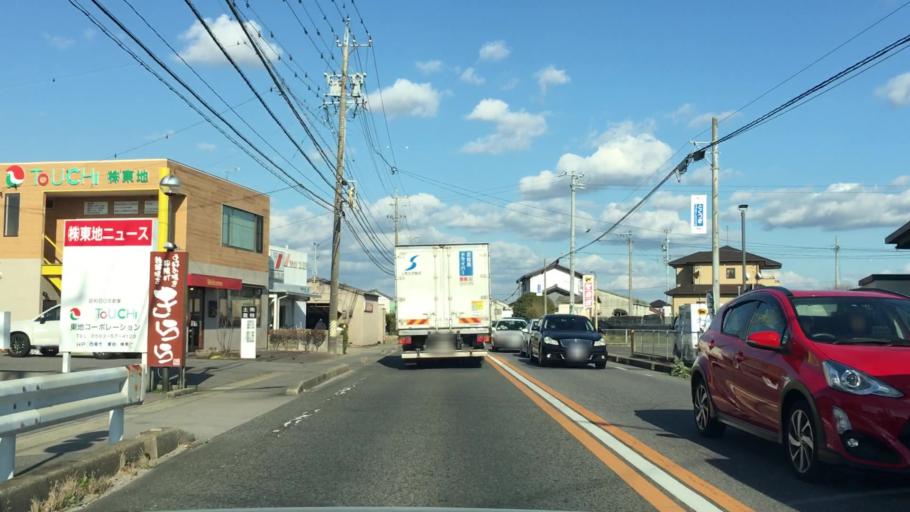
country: JP
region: Aichi
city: Nishio
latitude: 34.8721
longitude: 137.0743
